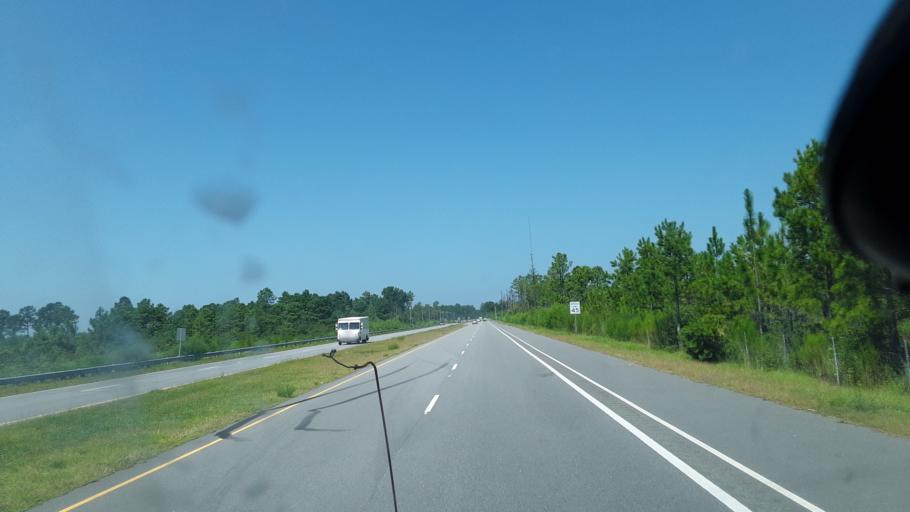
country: US
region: South Carolina
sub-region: Horry County
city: Forestbrook
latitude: 33.8117
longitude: -78.8989
